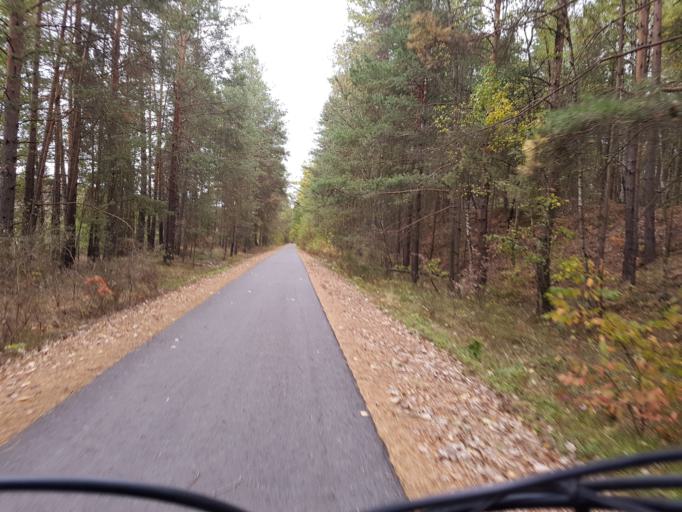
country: DE
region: Brandenburg
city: Trobitz
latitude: 51.5770
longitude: 13.4408
